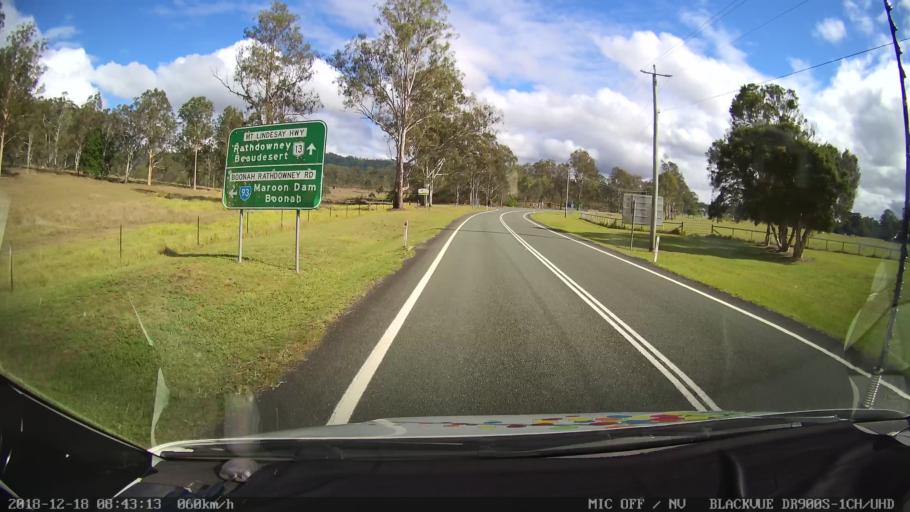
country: AU
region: Queensland
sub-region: Logan
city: Cedar Vale
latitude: -28.2200
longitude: 152.8583
